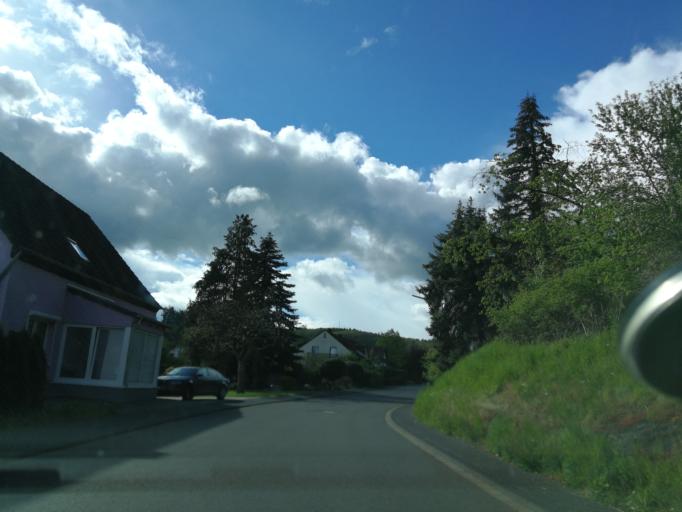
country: DE
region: Rheinland-Pfalz
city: Wittlich
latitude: 49.9986
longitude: 6.9098
